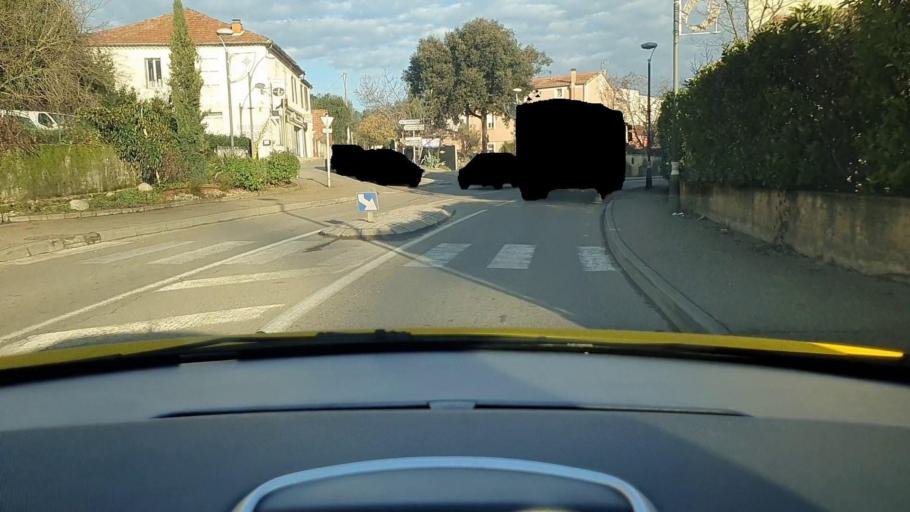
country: FR
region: Languedoc-Roussillon
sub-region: Departement du Gard
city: Saint-Martin-de-Valgalgues
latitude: 44.1593
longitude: 4.0829
